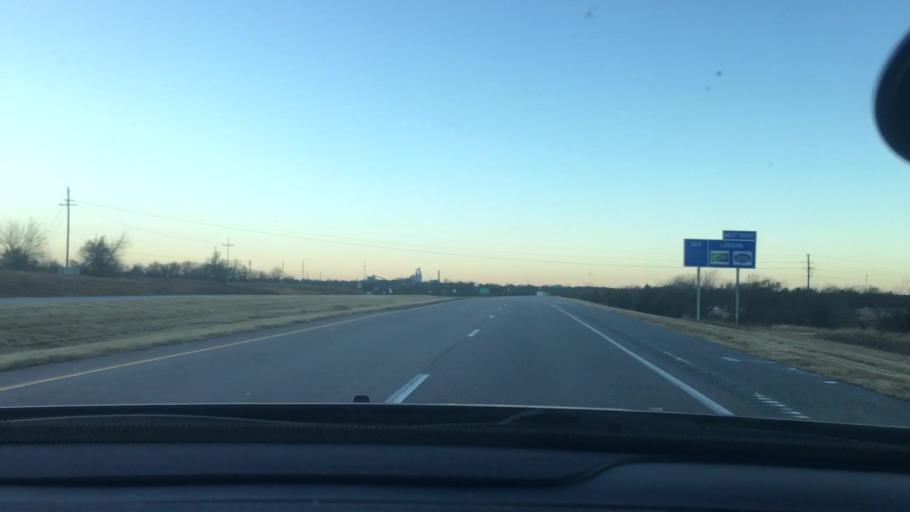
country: US
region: Oklahoma
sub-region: Pontotoc County
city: Ada
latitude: 34.8014
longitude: -96.6955
